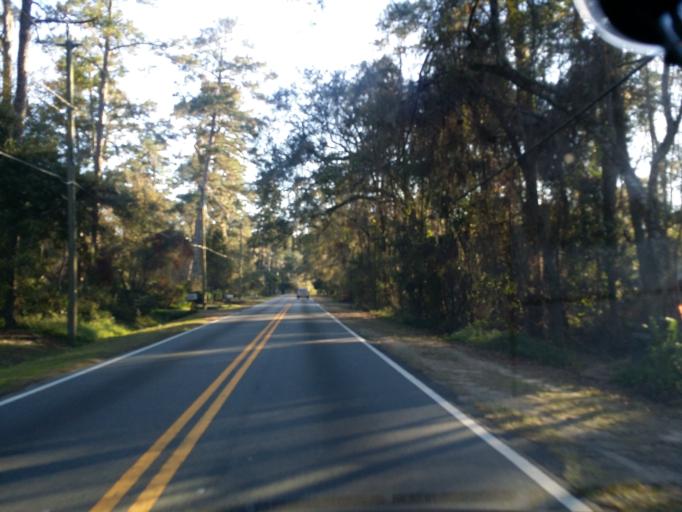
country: US
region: Florida
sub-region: Leon County
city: Tallahassee
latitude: 30.4265
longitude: -84.2620
